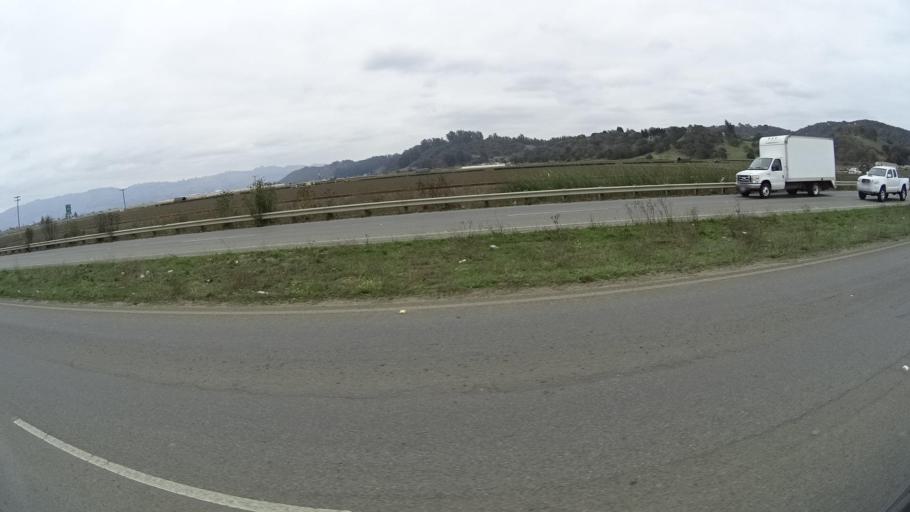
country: US
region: California
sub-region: Monterey County
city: Pajaro
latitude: 36.8861
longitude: -121.7479
